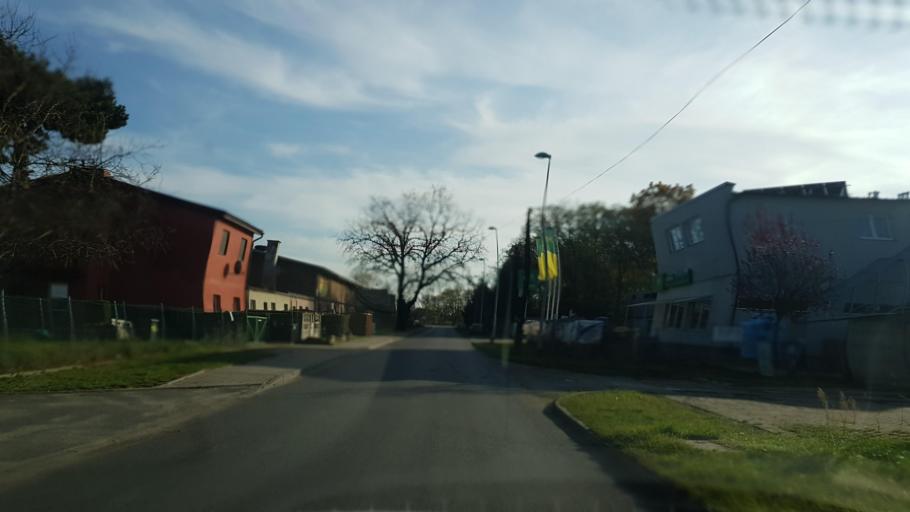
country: PL
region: West Pomeranian Voivodeship
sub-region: Powiat policki
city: Dobra
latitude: 53.4878
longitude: 14.3801
